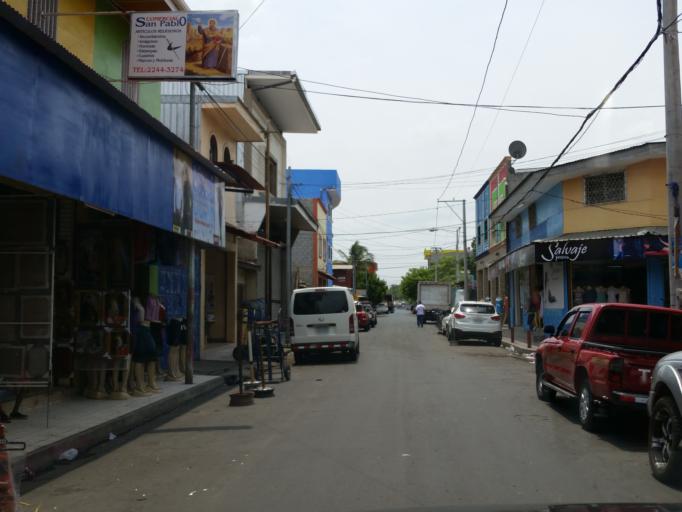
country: NI
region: Managua
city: Managua
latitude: 12.1503
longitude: -86.2567
